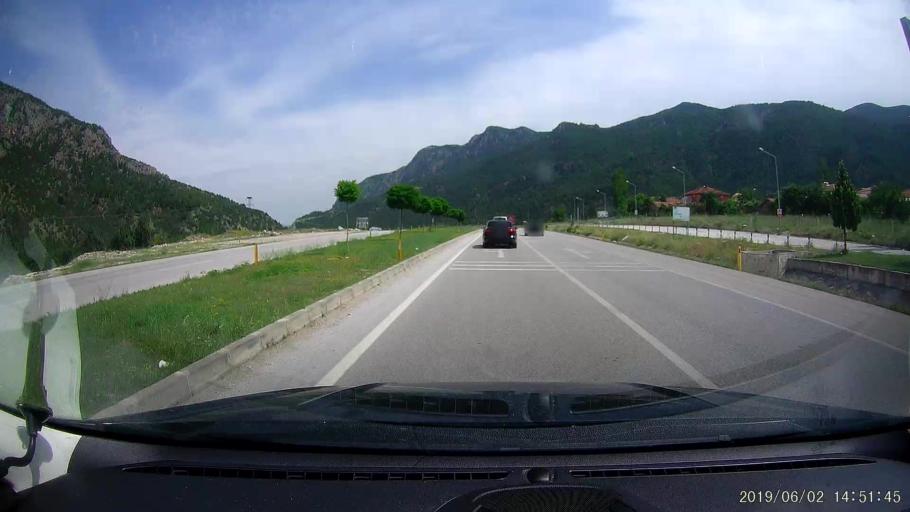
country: TR
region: Corum
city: Kargi
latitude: 41.0553
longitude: 34.5440
